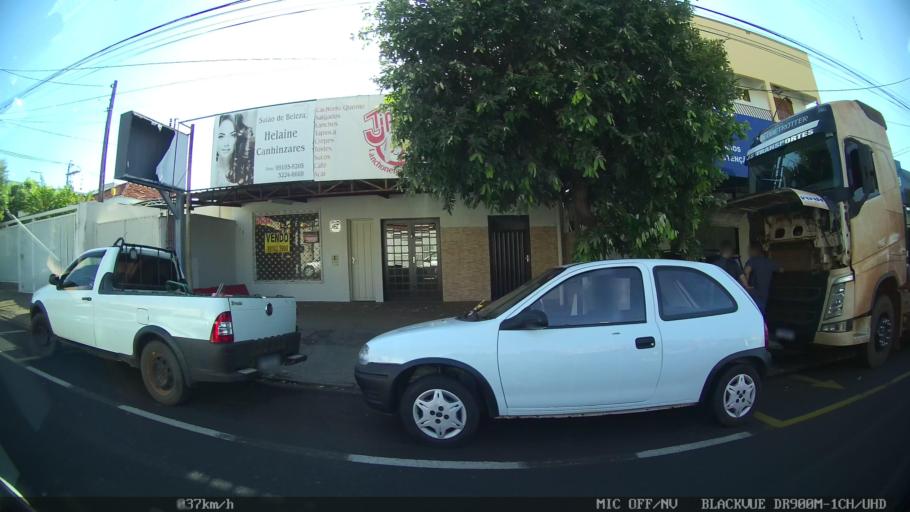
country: BR
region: Sao Paulo
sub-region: Sao Jose Do Rio Preto
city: Sao Jose do Rio Preto
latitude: -20.7889
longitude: -49.3585
